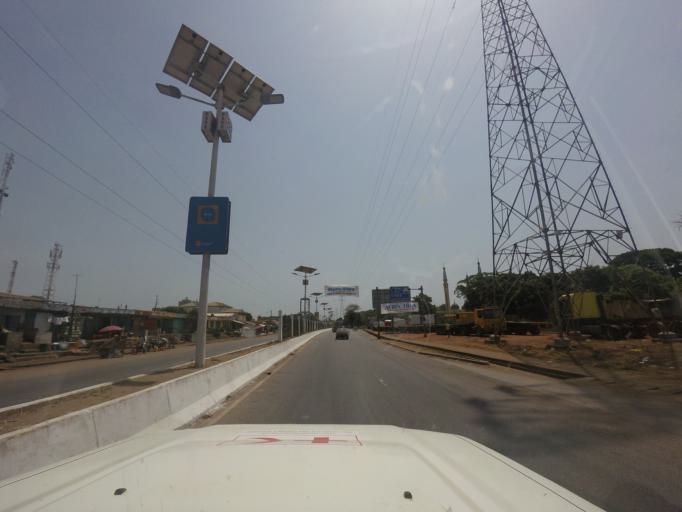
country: GN
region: Conakry
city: Conakry
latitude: 9.5345
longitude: -13.6812
